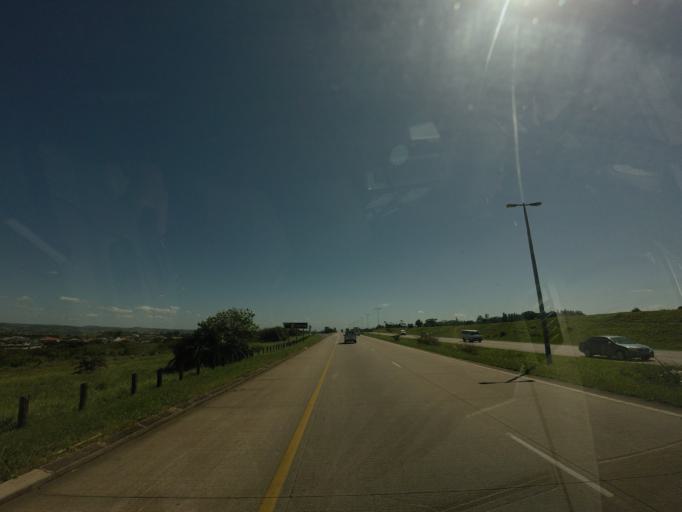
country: ZA
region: KwaZulu-Natal
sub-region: iLembe District Municipality
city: Stanger
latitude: -29.4113
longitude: 31.2800
